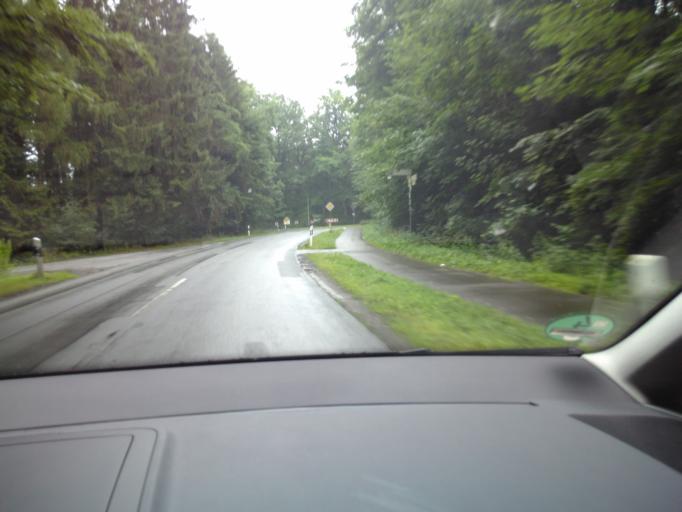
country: DE
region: North Rhine-Westphalia
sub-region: Regierungsbezirk Detmold
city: Oerlinghausen
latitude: 51.8987
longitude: 8.5998
